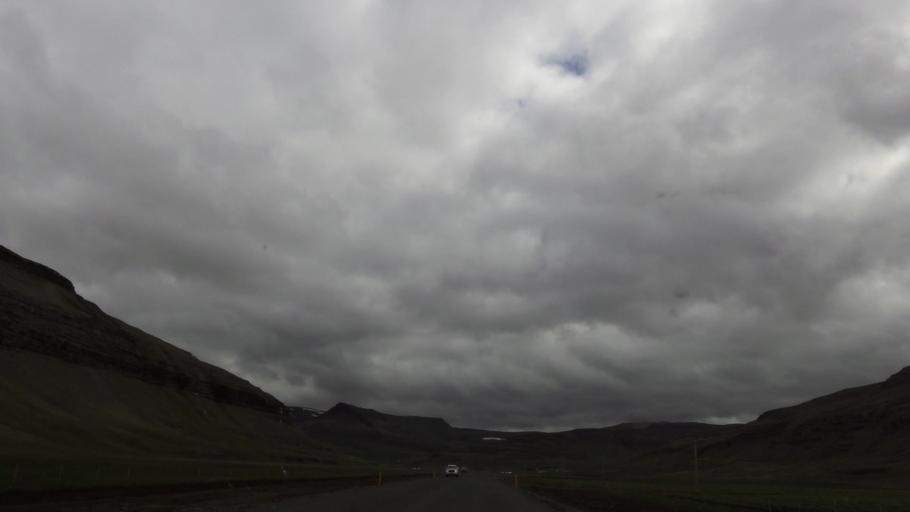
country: IS
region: West
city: Borgarnes
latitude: 65.3678
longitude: -21.8453
